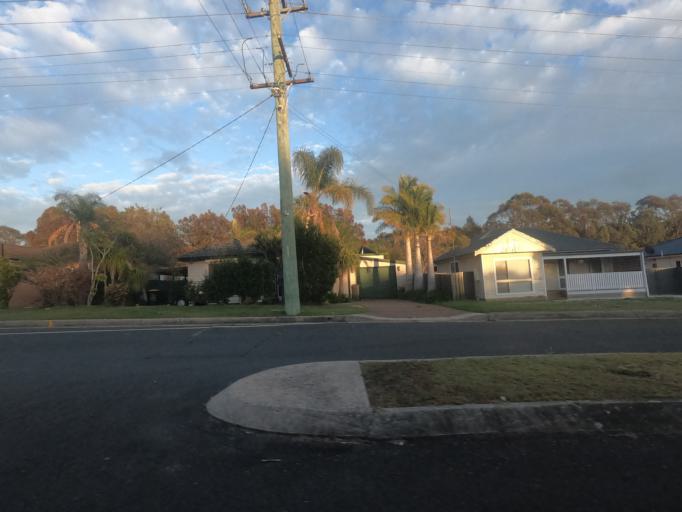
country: AU
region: New South Wales
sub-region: Wollongong
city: Dapto
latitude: -34.5033
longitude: 150.7942
